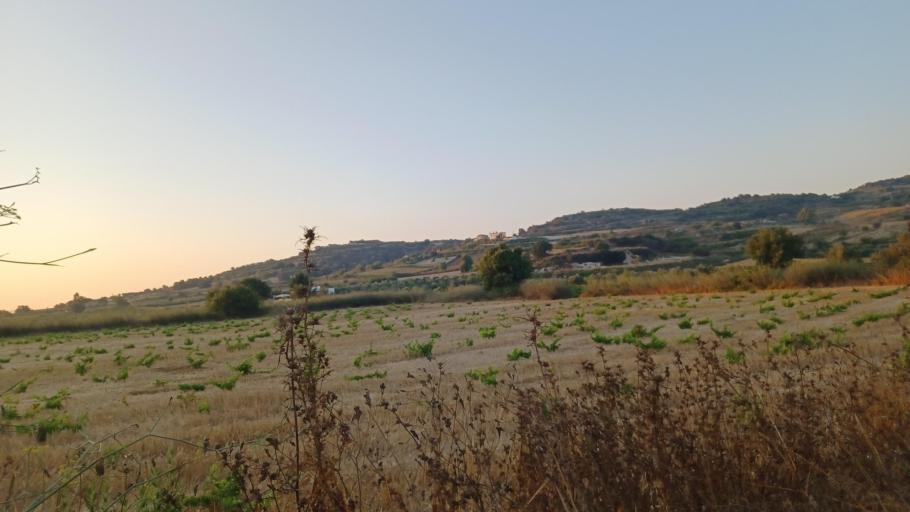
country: CY
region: Pafos
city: Mesogi
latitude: 34.8731
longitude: 32.5007
